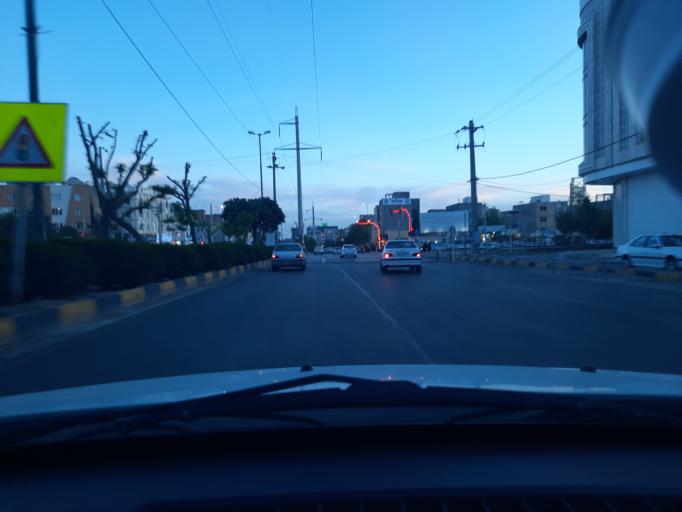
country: IR
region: Qazvin
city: Qazvin
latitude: 36.3026
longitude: 50.0104
